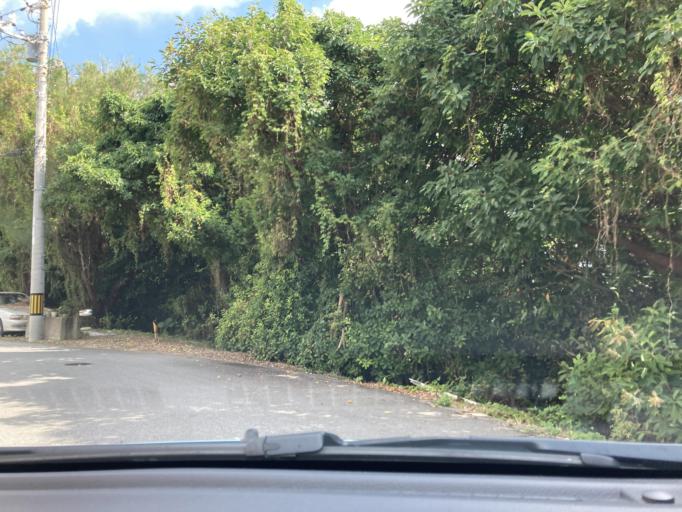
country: JP
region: Okinawa
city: Itoman
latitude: 26.1289
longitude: 127.7755
